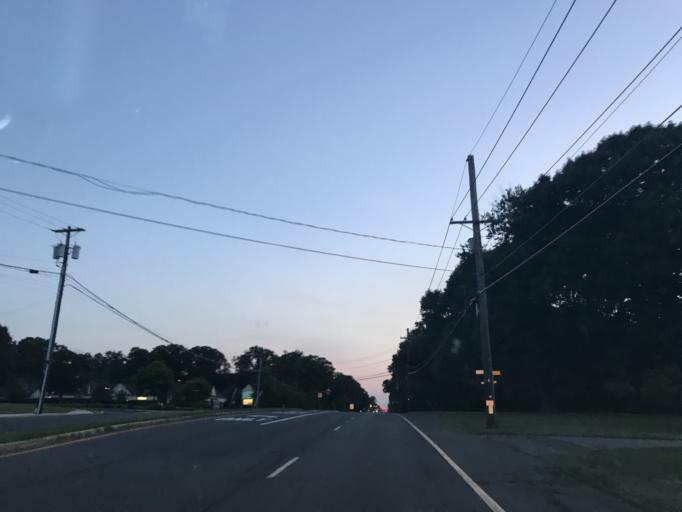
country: US
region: New Jersey
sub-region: Burlington County
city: Roebling
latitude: 40.1118
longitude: -74.7714
